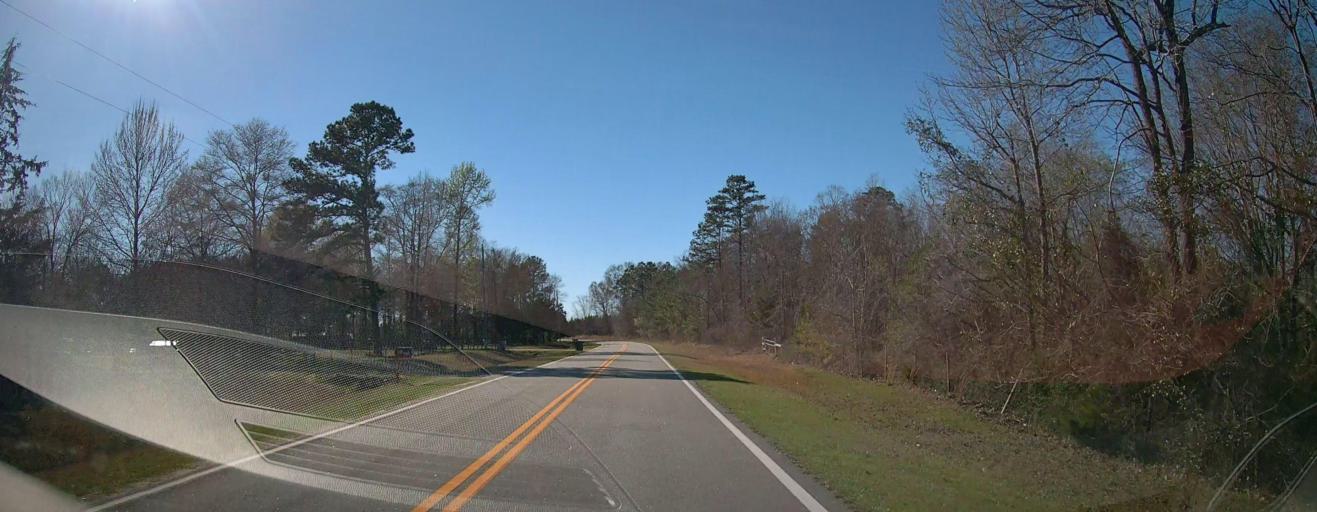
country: US
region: Georgia
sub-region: Peach County
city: Byron
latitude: 32.6745
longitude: -83.8316
